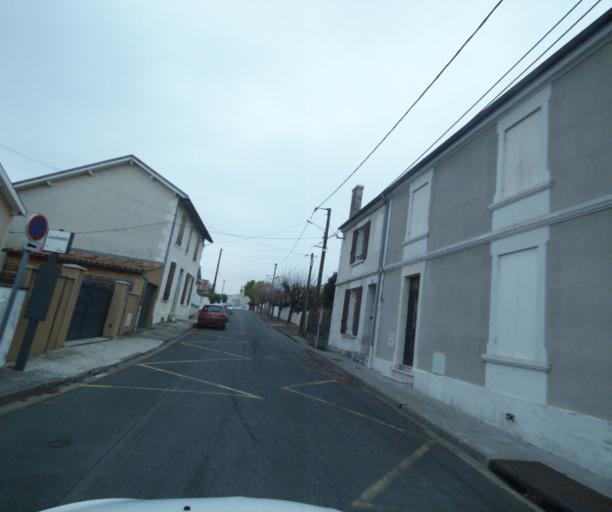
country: FR
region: Poitou-Charentes
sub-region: Departement de la Charente-Maritime
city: Saintes
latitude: 45.7441
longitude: -0.6110
